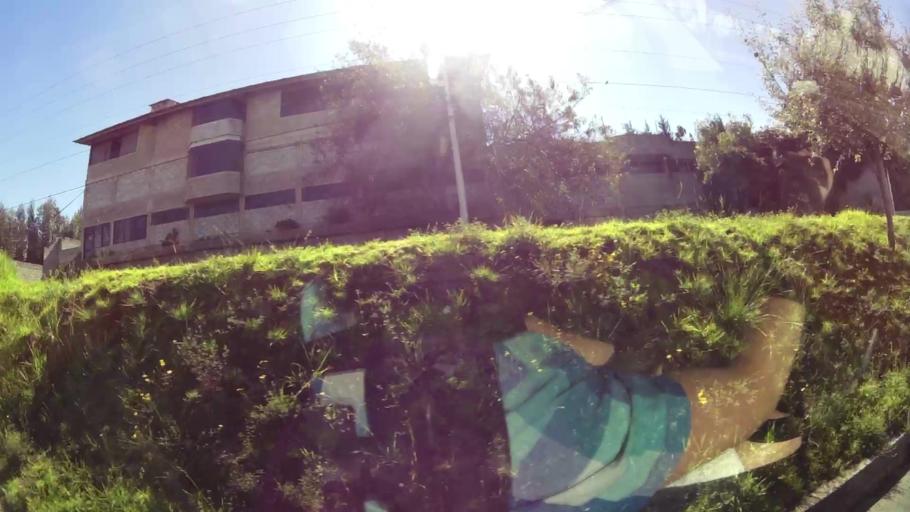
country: EC
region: Pichincha
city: Quito
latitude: -0.1245
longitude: -78.4764
